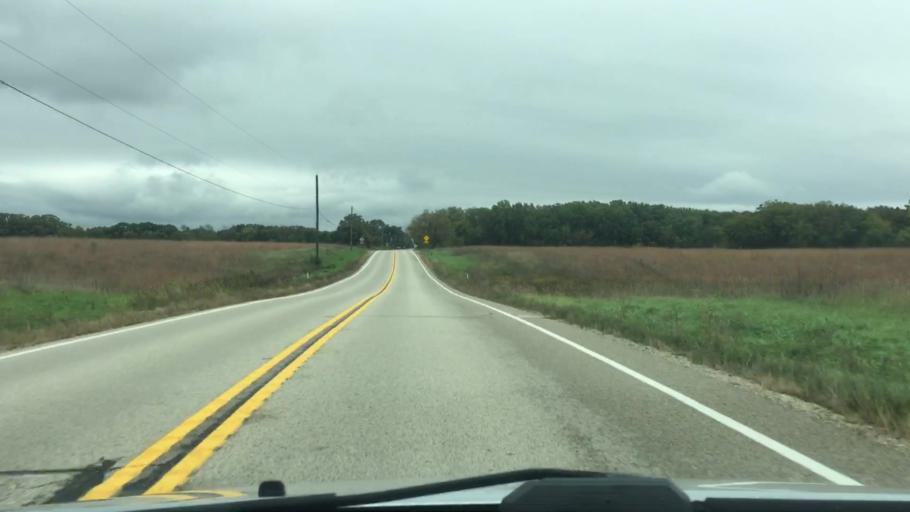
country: US
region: Wisconsin
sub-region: Waukesha County
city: Eagle
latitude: 42.8914
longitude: -88.4737
